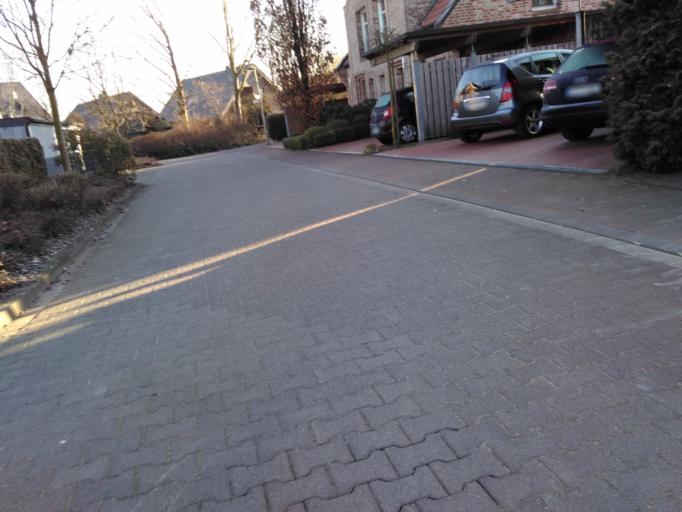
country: DE
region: North Rhine-Westphalia
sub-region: Regierungsbezirk Detmold
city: Verl
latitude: 51.8720
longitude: 8.4981
